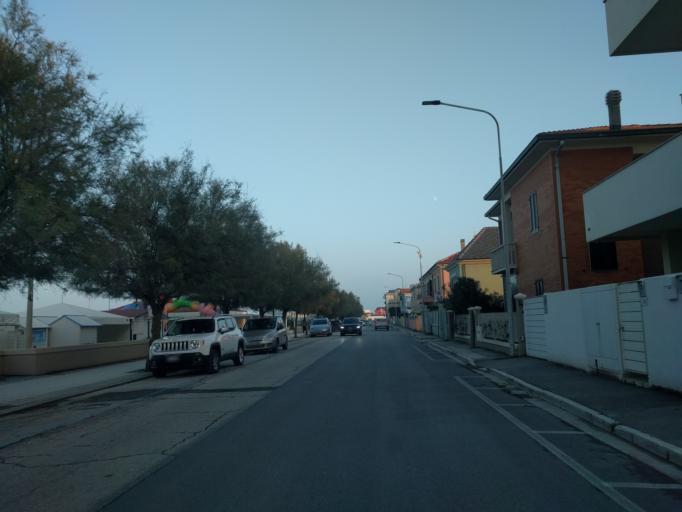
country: IT
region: The Marches
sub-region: Provincia di Ancona
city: Senigallia
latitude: 43.7219
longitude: 13.2160
